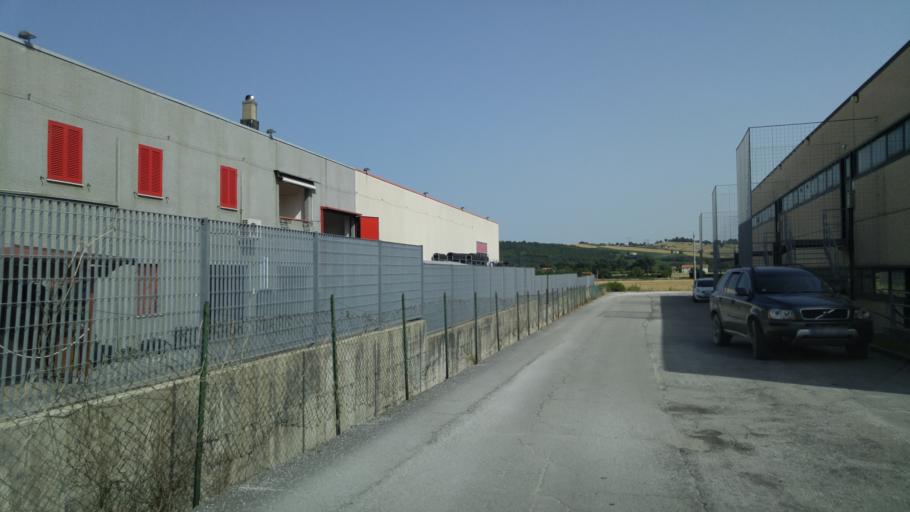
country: IT
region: The Marches
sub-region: Provincia di Ancona
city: Monterado
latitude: 43.7215
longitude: 13.0889
